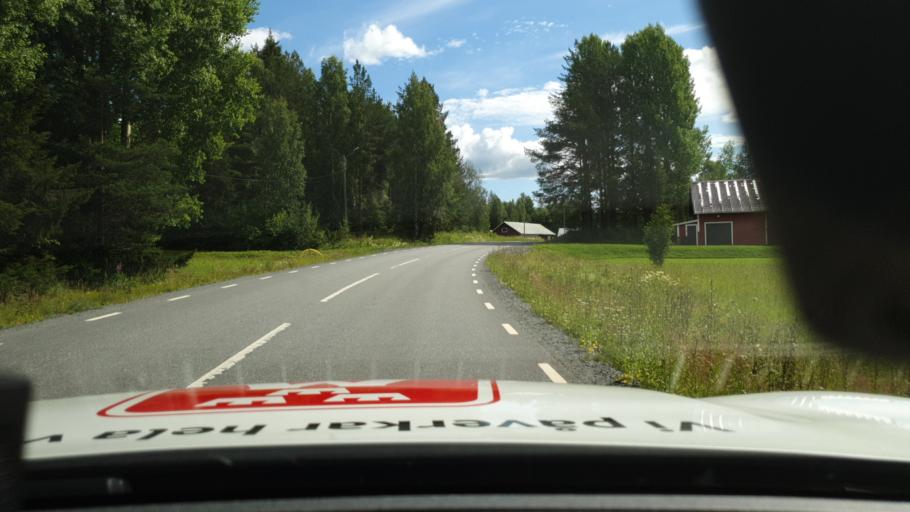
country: SE
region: Norrbotten
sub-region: Lulea Kommun
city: Sodra Sunderbyn
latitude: 65.8310
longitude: 21.9644
